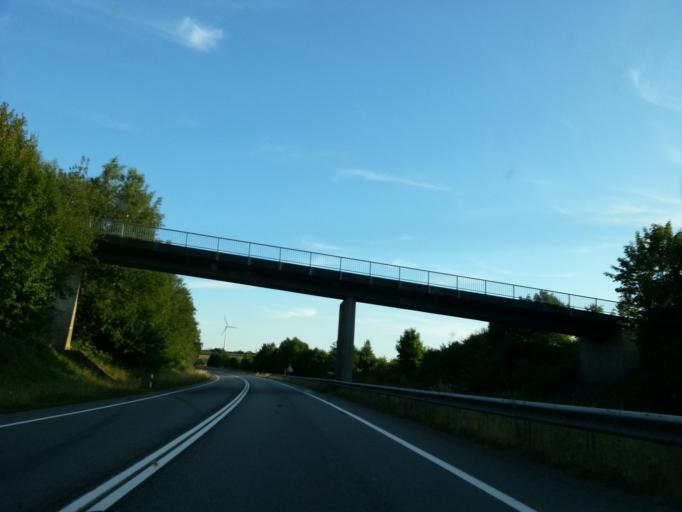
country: DE
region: Rheinland-Pfalz
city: Weselberg
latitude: 49.3412
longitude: 7.6009
